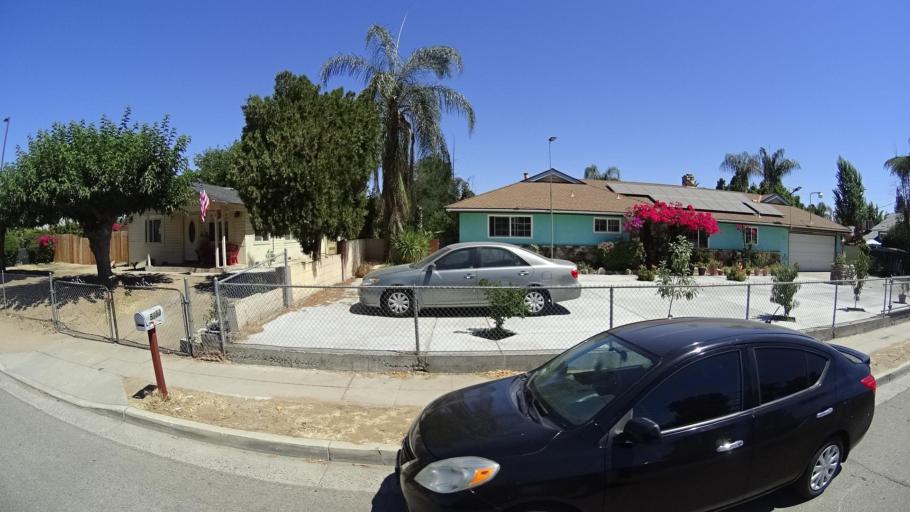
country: US
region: California
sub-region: Fresno County
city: Sunnyside
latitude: 36.7432
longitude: -119.7156
